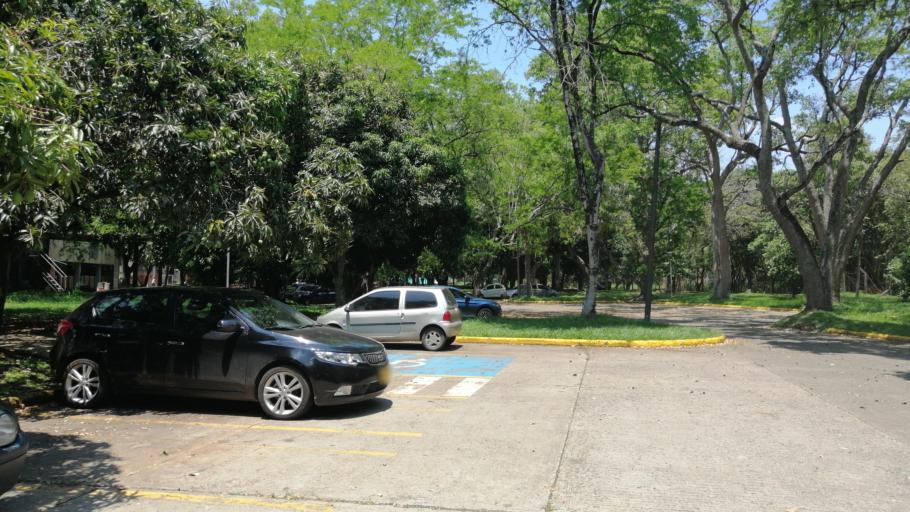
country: CO
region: Valle del Cauca
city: Cali
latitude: 3.3742
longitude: -76.5316
